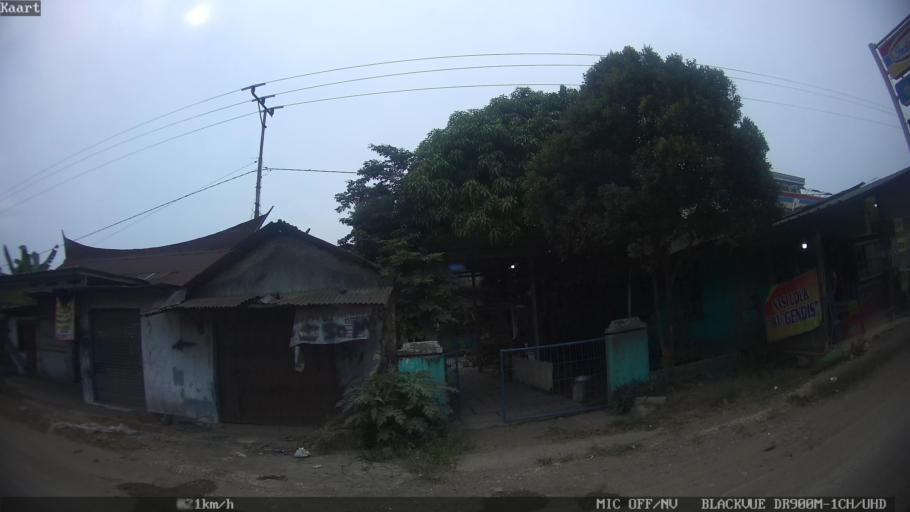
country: ID
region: Lampung
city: Panjang
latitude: -5.4268
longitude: 105.3291
